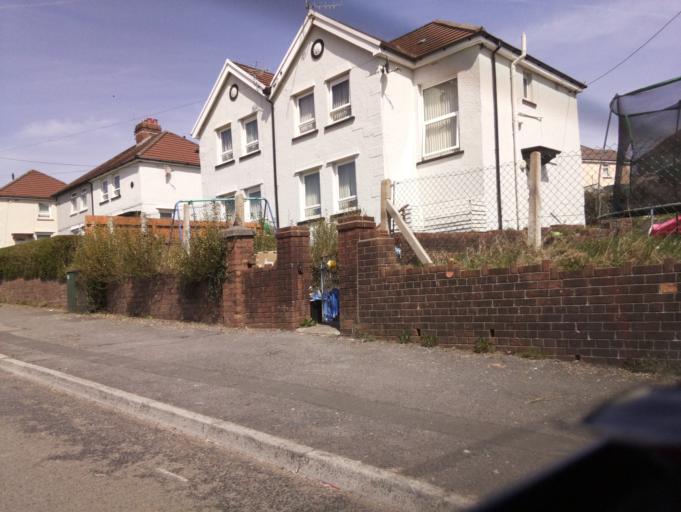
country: GB
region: Wales
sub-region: Merthyr Tydfil County Borough
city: Merthyr Tydfil
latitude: 51.7618
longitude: -3.3721
